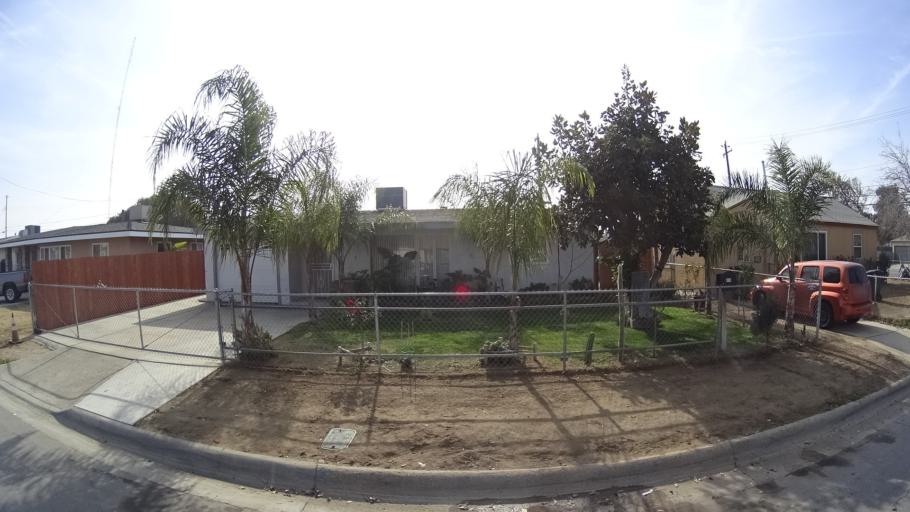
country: US
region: California
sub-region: Kern County
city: Bakersfield
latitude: 35.3489
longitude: -119.0115
